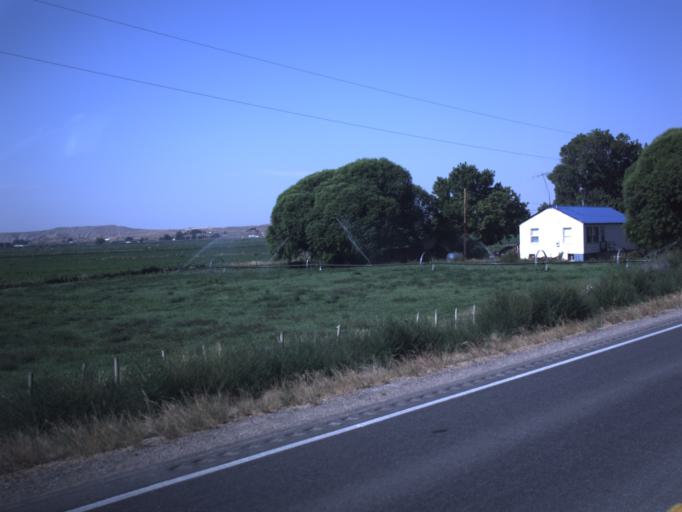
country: US
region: Utah
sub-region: Uintah County
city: Naples
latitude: 40.3695
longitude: -109.3678
